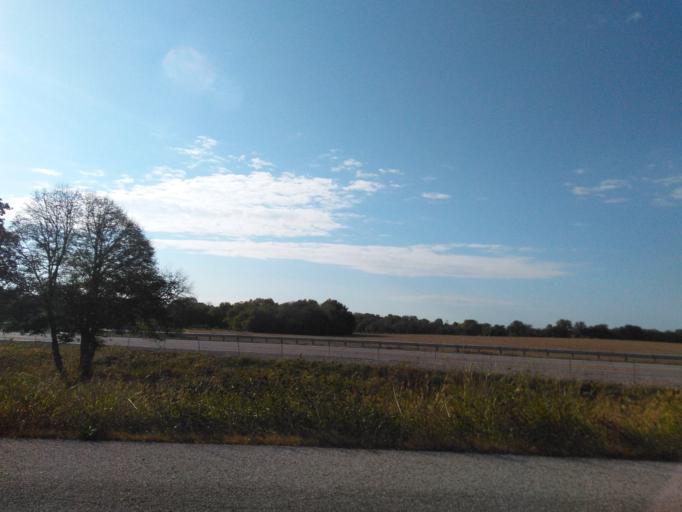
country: US
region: Illinois
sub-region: Bond County
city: Greenville
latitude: 38.8545
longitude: -89.4548
